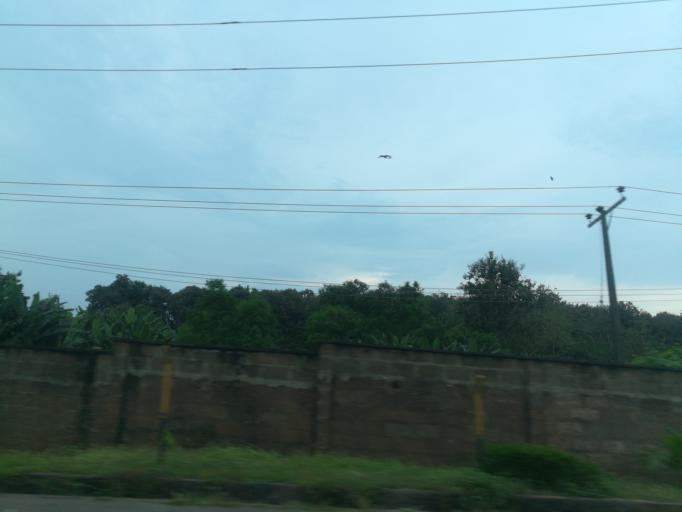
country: NG
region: Oyo
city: Moniya
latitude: 7.4555
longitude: 3.9071
